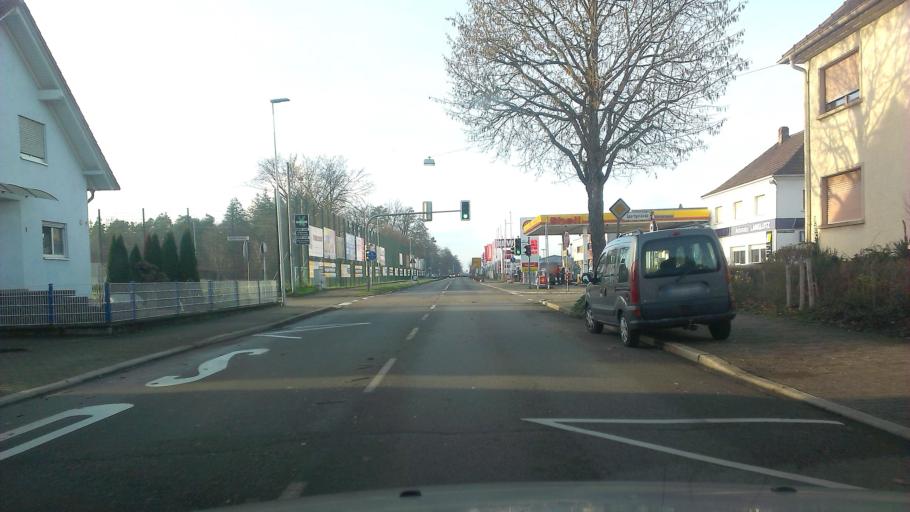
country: DE
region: Baden-Wuerttemberg
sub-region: Karlsruhe Region
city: Waghausel
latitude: 49.2452
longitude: 8.5374
